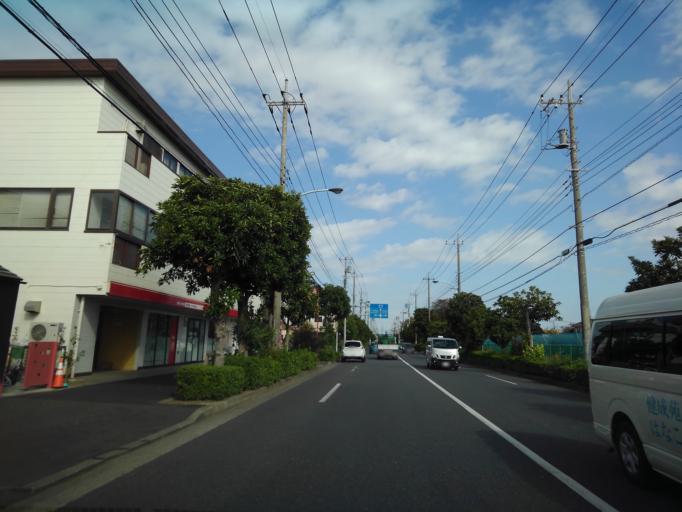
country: JP
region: Tokyo
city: Kokubunji
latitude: 35.7210
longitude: 139.4973
